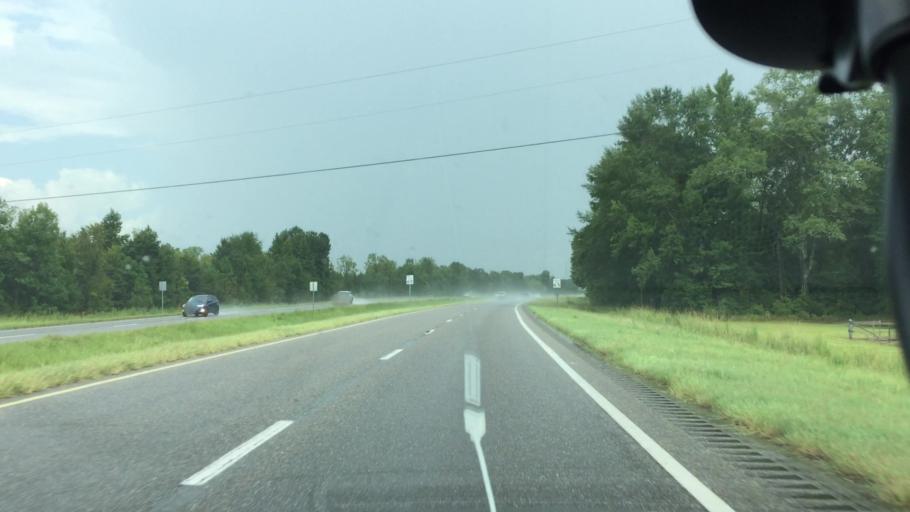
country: US
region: Alabama
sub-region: Montgomery County
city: Pike Road
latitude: 32.2442
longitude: -86.1358
